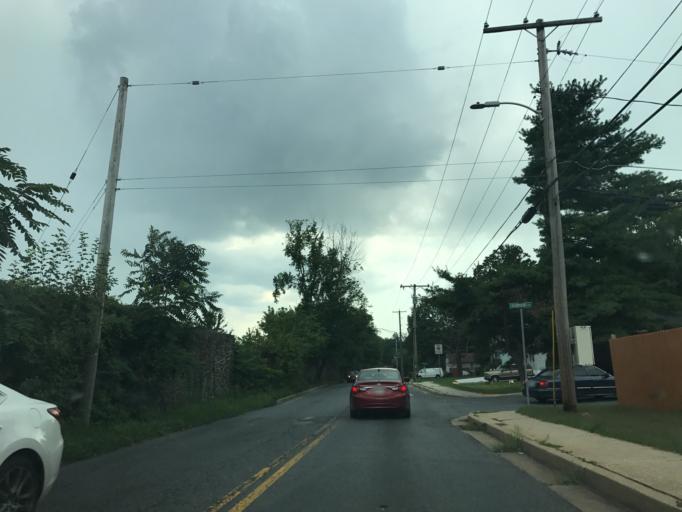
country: US
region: Maryland
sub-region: Baltimore County
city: Lochearn
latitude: 39.3500
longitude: -76.7108
